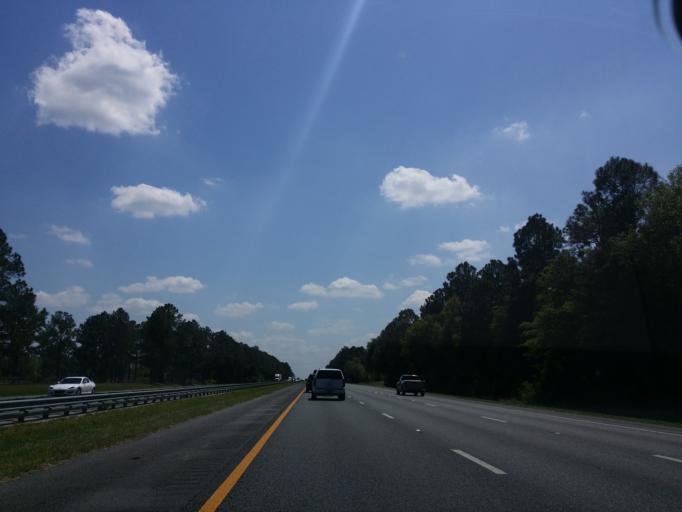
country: US
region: Florida
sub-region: Columbia County
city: Lake City
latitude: 30.1616
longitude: -82.6794
